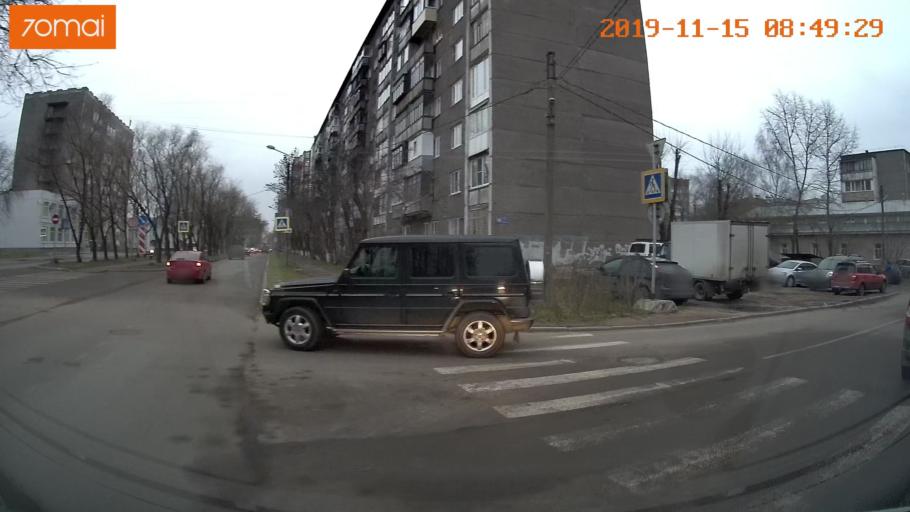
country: RU
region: Vologda
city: Cherepovets
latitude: 59.1237
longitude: 37.9221
